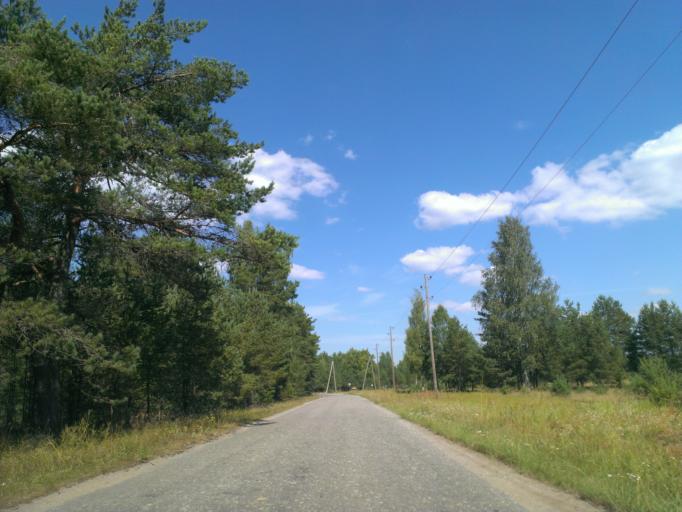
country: LV
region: Adazi
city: Adazi
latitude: 57.1159
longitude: 24.3626
